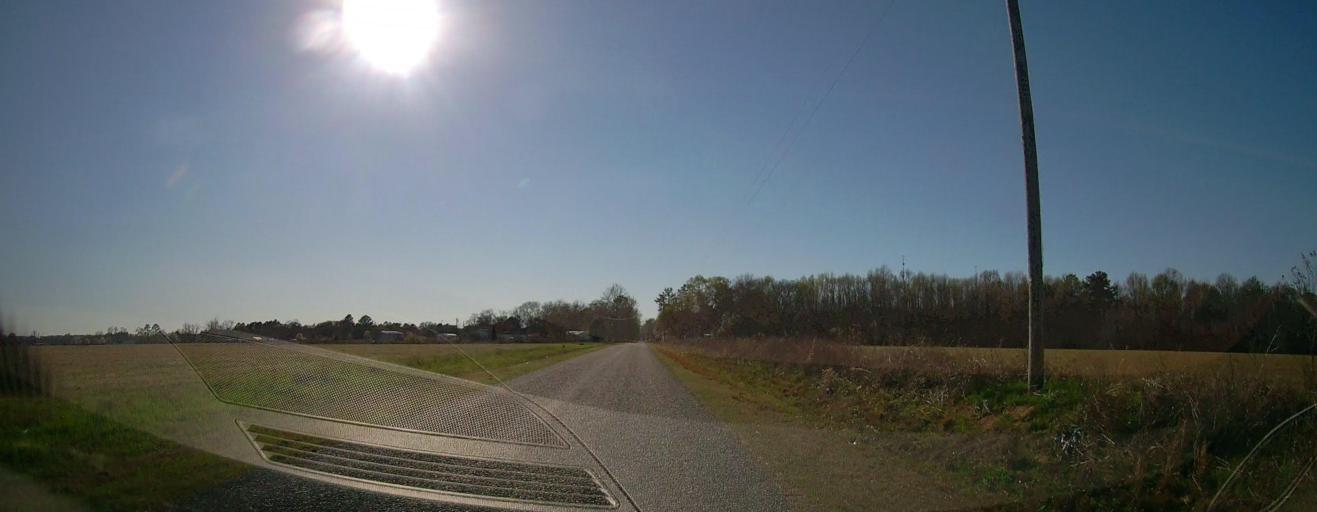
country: US
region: Georgia
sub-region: Taylor County
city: Reynolds
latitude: 32.5550
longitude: -84.0839
